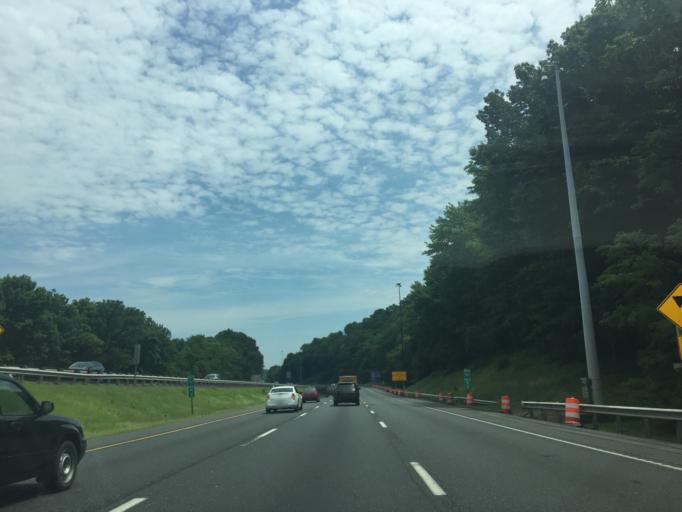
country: US
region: Maryland
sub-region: Harford County
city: Havre de Grace
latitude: 39.5765
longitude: -76.1191
